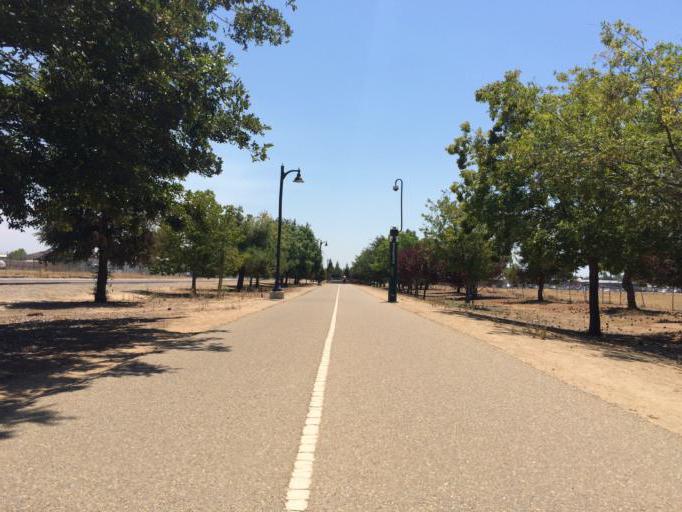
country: US
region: California
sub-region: Fresno County
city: Clovis
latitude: 36.8392
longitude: -119.7105
